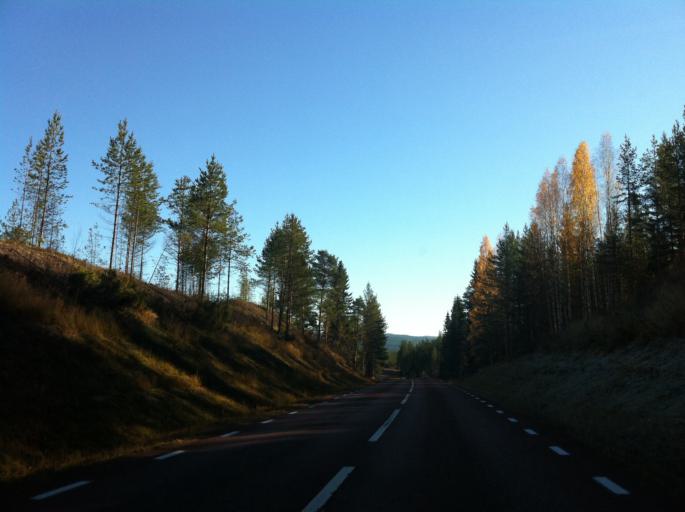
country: SE
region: Dalarna
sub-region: Alvdalens Kommun
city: AElvdalen
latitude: 61.3079
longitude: 13.7185
